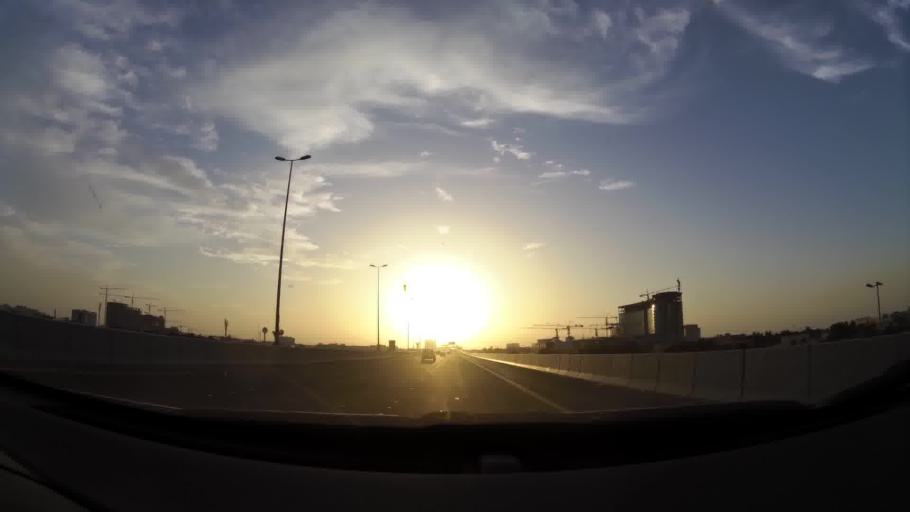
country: KW
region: Al Asimah
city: Ar Rabiyah
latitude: 29.3331
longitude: 47.9109
